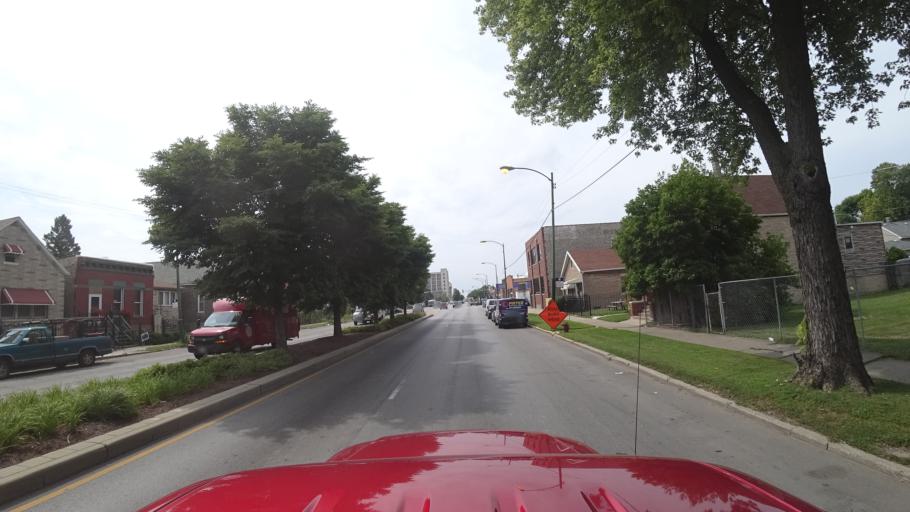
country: US
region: Illinois
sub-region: Cook County
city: Chicago
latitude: 41.8319
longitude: -87.6657
